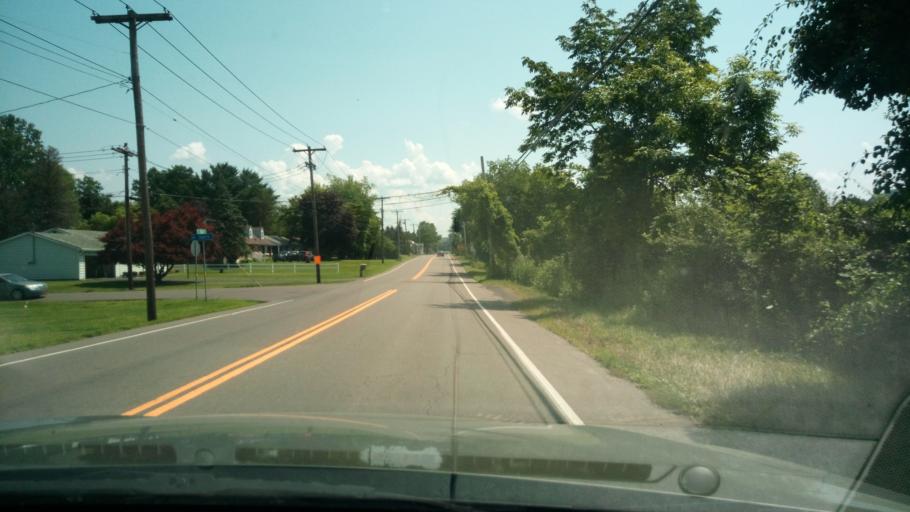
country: US
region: New York
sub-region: Chemung County
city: Horseheads North
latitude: 42.1902
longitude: -76.8186
